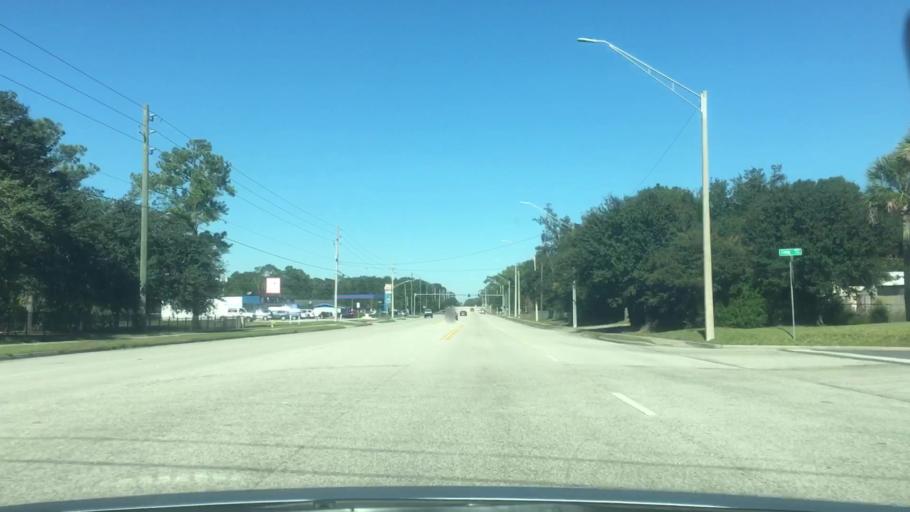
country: US
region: Florida
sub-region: Duval County
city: Atlantic Beach
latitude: 30.3363
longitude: -81.5233
